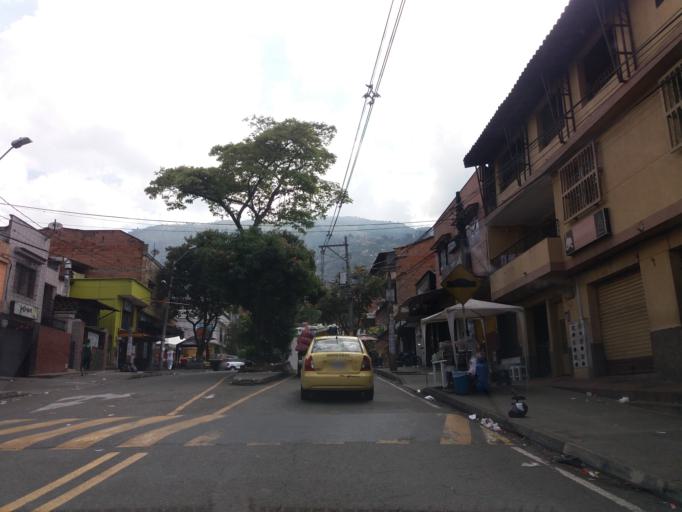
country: CO
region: Antioquia
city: Medellin
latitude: 6.2833
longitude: -75.5573
